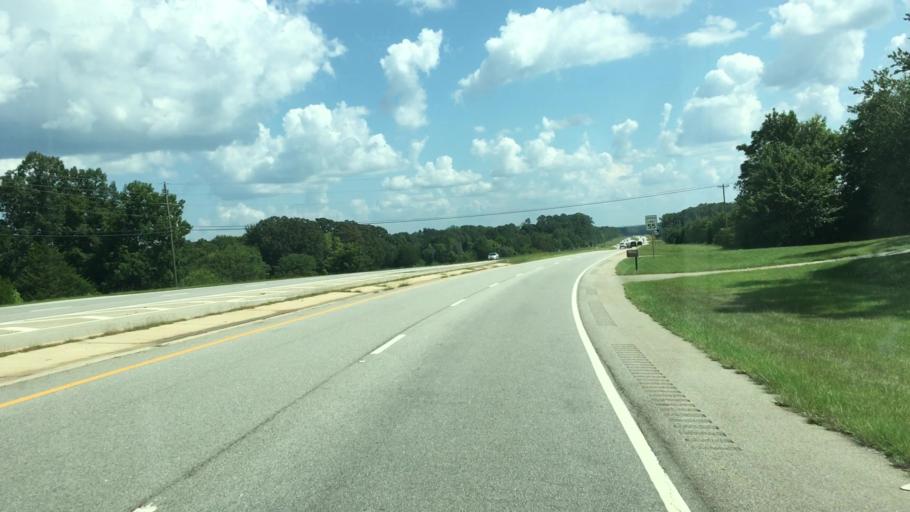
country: US
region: Georgia
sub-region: Putnam County
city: Eatonton
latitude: 33.2674
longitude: -83.3360
